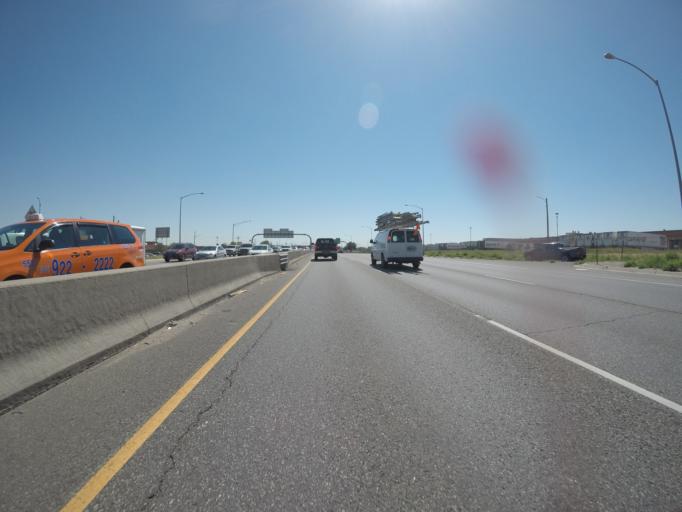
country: US
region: Colorado
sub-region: Adams County
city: Commerce City
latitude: 39.7800
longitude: -104.9395
